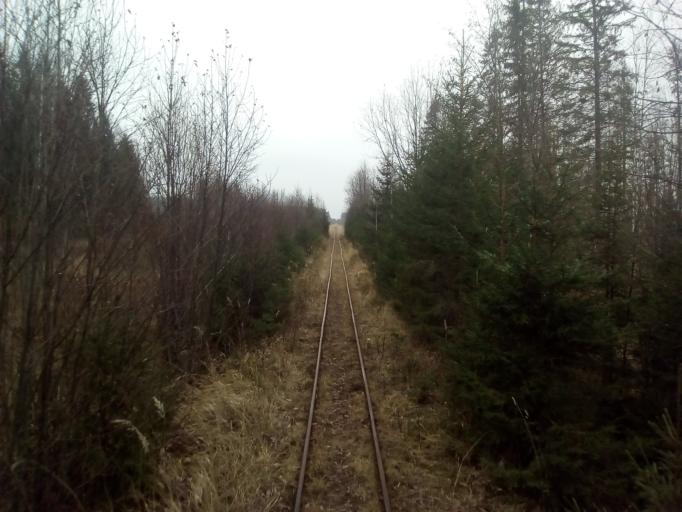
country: RU
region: Vologda
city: Kharovsk
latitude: 59.8030
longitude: 40.4546
